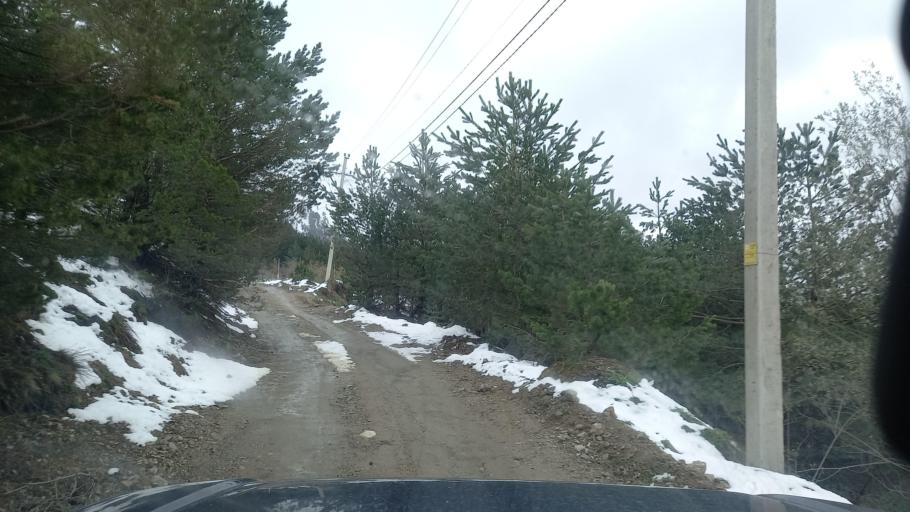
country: RU
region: North Ossetia
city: Mizur
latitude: 42.8076
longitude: 43.9578
